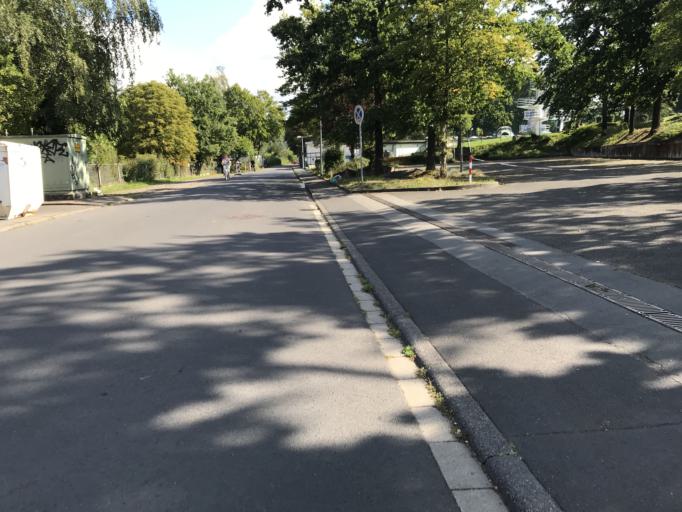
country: DE
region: Hesse
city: Witzenhausen
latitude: 51.3457
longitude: 9.8641
